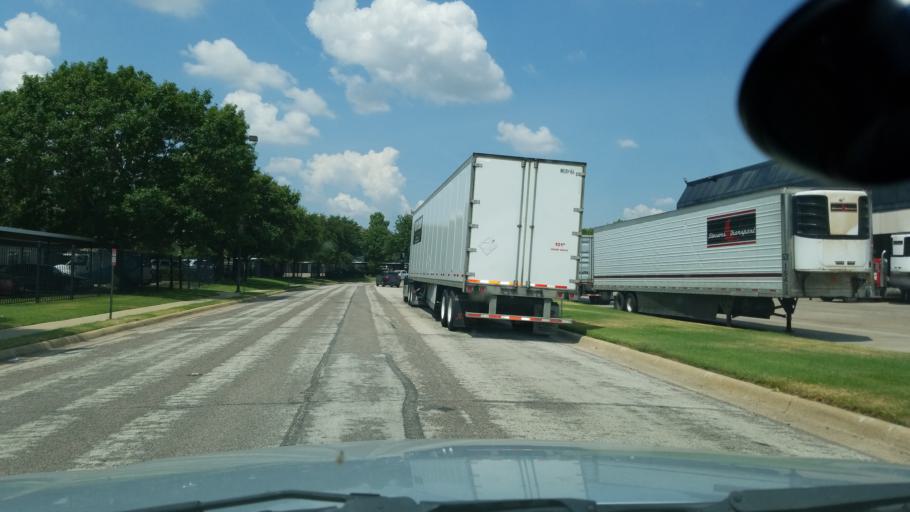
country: US
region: Texas
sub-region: Dallas County
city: Farmers Branch
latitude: 32.8595
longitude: -96.8991
